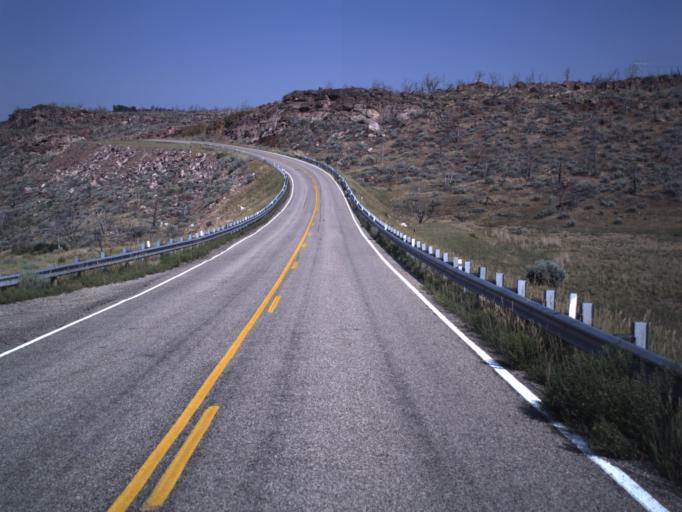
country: US
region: Utah
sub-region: Daggett County
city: Manila
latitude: 40.9412
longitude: -109.4133
